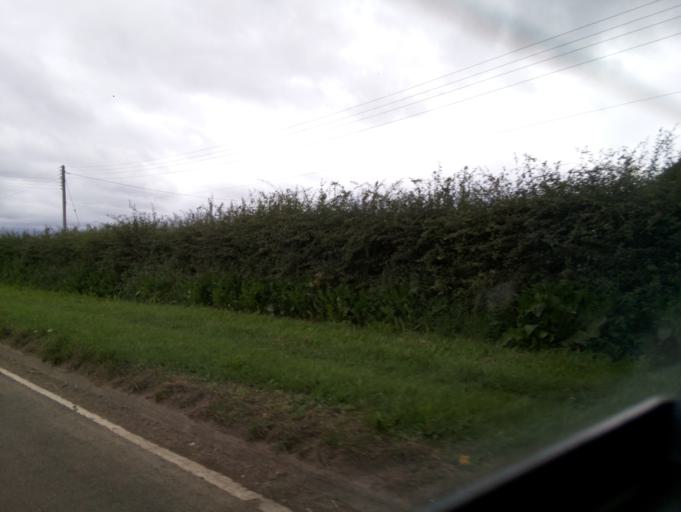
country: GB
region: England
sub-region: Worcestershire
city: Kempsey
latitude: 52.1280
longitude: -2.2168
